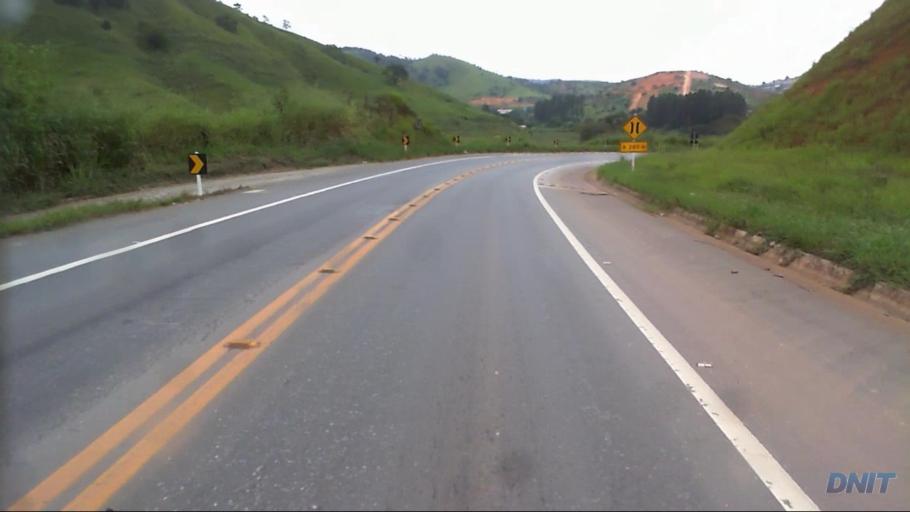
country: BR
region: Minas Gerais
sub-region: Nova Era
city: Nova Era
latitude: -19.7415
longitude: -43.0196
